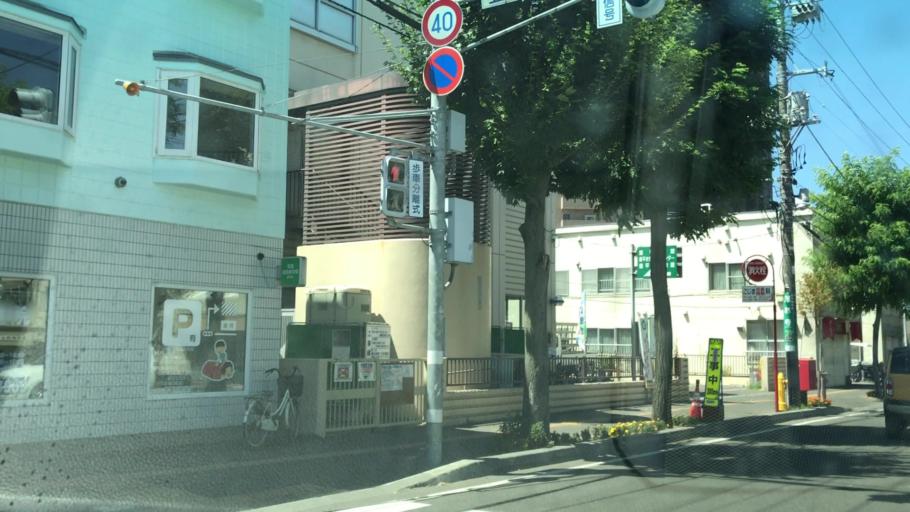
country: JP
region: Hokkaido
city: Sapporo
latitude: 43.0478
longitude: 141.3723
